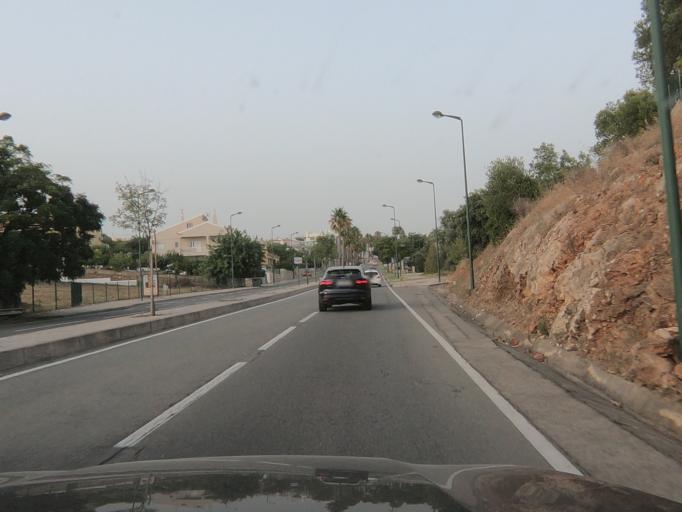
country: PT
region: Faro
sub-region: Loule
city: Loule
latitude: 37.1339
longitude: -8.0350
